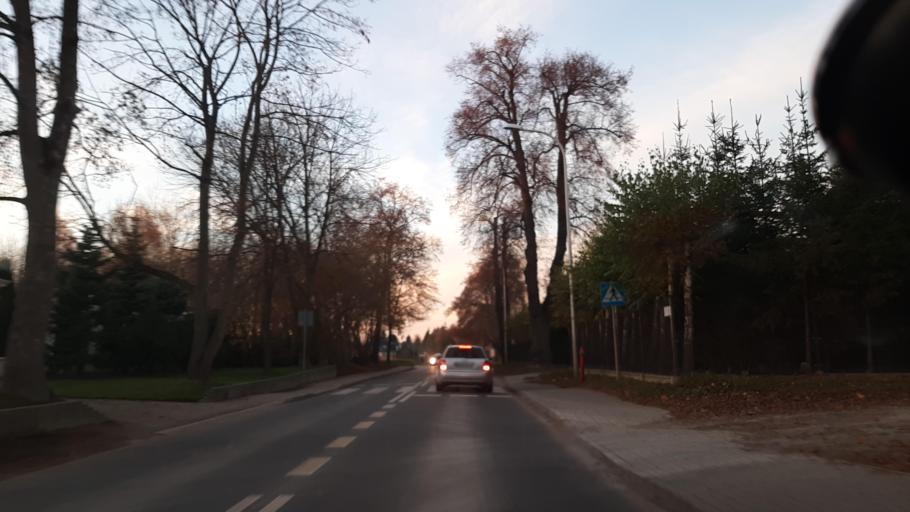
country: PL
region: Lublin Voivodeship
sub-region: Powiat lubelski
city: Jastkow
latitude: 51.2830
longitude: 22.5013
